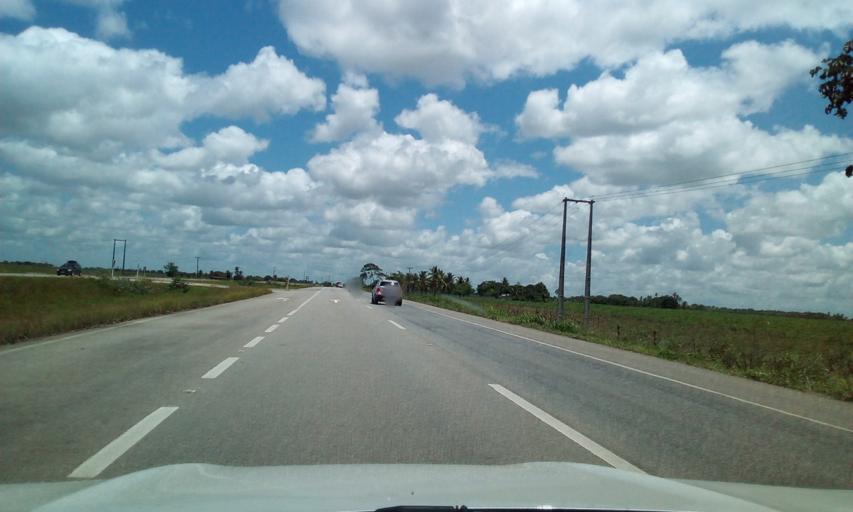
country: BR
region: Alagoas
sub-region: Junqueiro
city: Junqueiro
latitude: -9.8875
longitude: -36.3929
